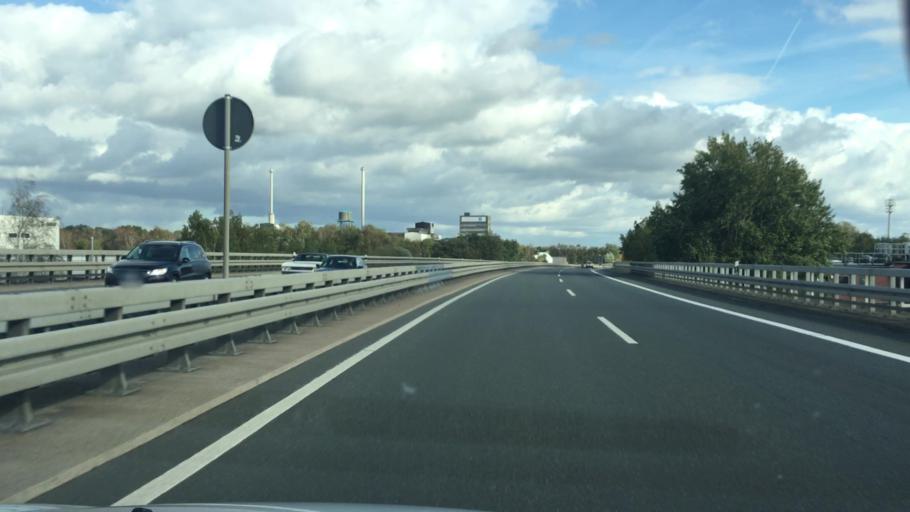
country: DE
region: Lower Saxony
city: Nienburg
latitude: 52.6584
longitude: 9.2054
